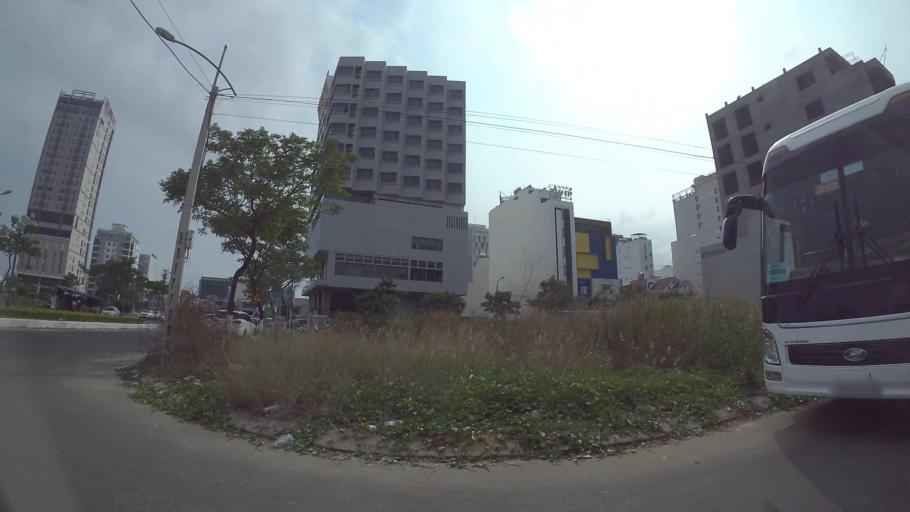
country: VN
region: Da Nang
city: Son Tra
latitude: 16.0714
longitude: 108.2382
